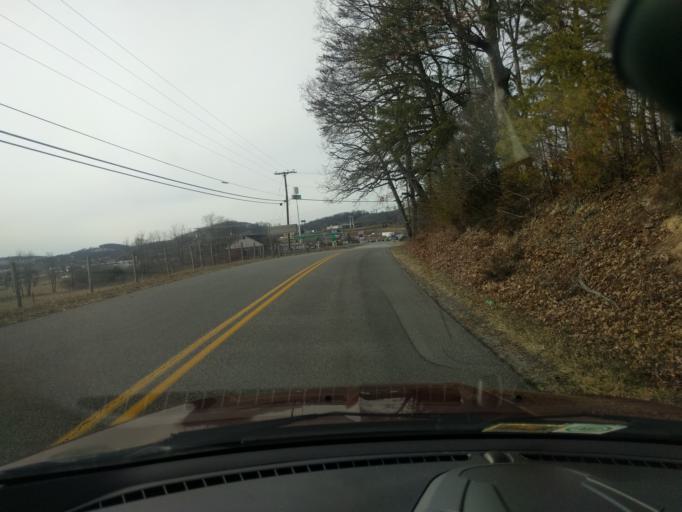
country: US
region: Virginia
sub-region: Augusta County
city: Stuarts Draft
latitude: 37.9306
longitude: -79.2234
